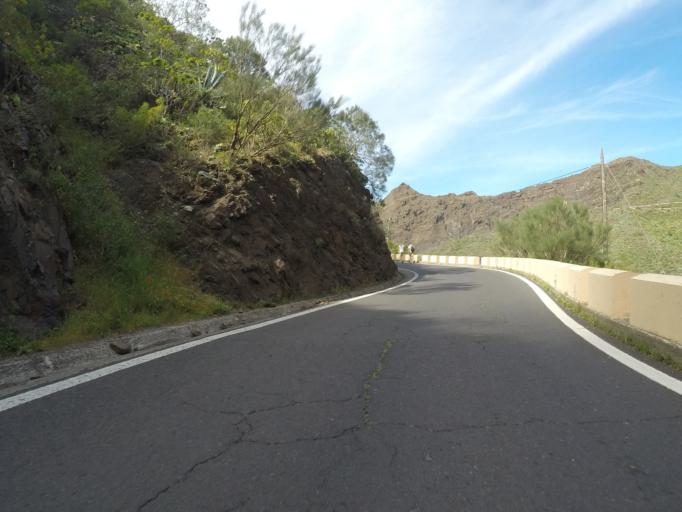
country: ES
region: Canary Islands
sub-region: Provincia de Santa Cruz de Tenerife
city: Santiago del Teide
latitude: 28.3079
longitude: -16.8399
